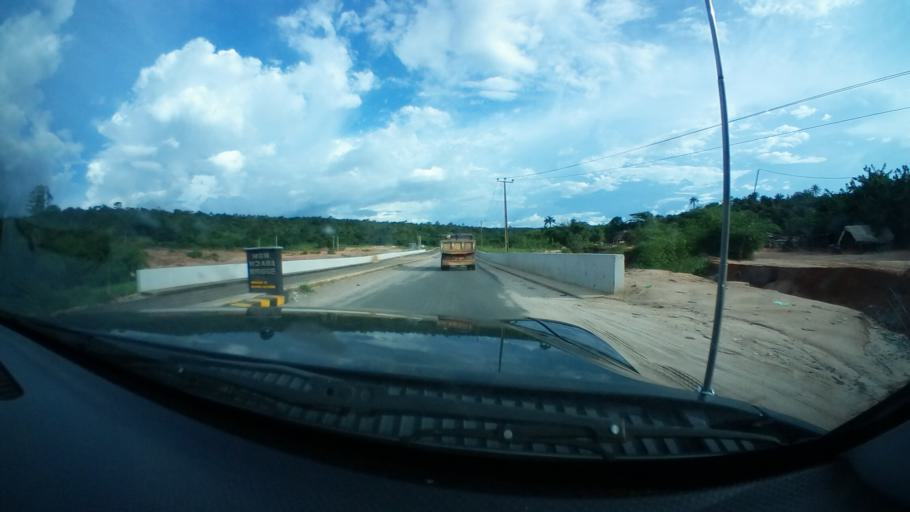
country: NG
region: Imo
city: Orodo
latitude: 5.7018
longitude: 7.0101
